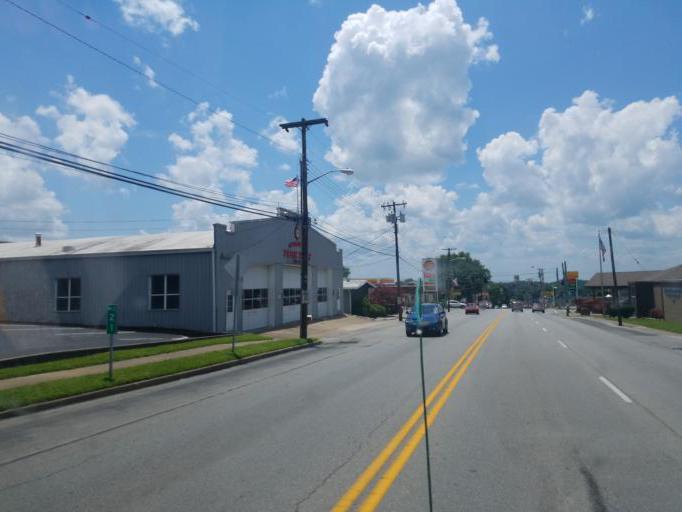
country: US
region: Kentucky
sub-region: Grayson County
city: Leitchfield
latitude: 37.4784
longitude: -86.2940
